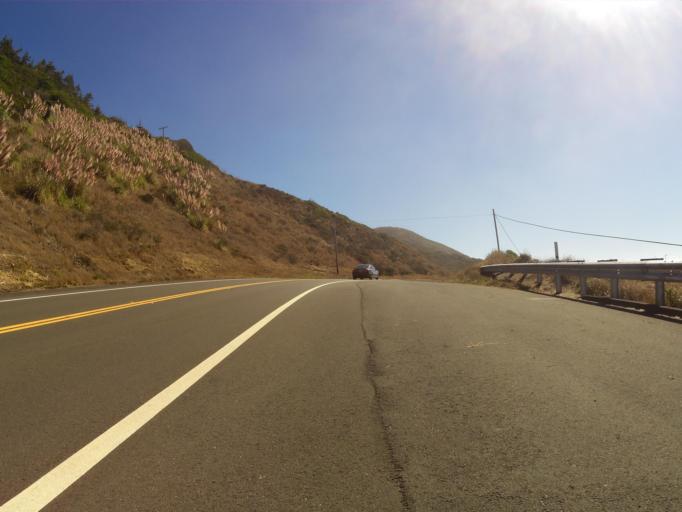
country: US
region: California
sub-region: Mendocino County
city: Fort Bragg
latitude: 39.6101
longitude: -123.7825
